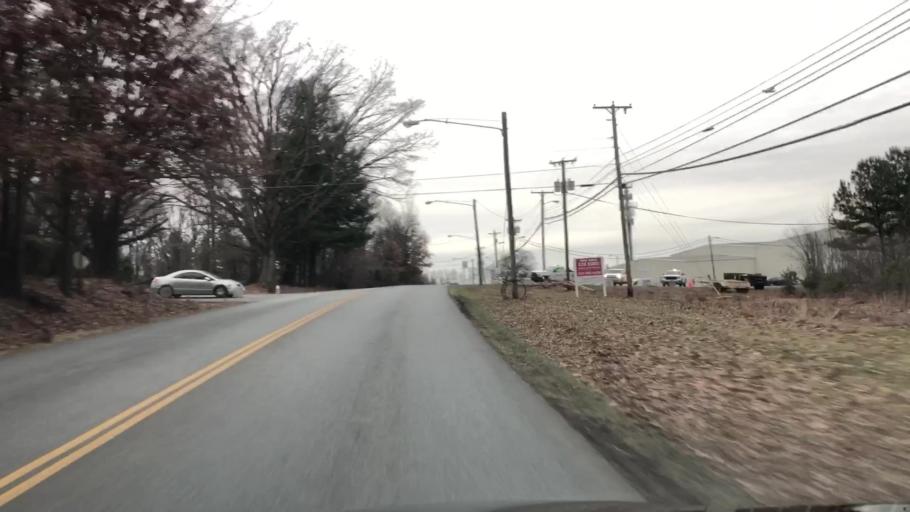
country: US
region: Virginia
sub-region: City of Lynchburg
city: West Lynchburg
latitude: 37.3516
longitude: -79.1912
